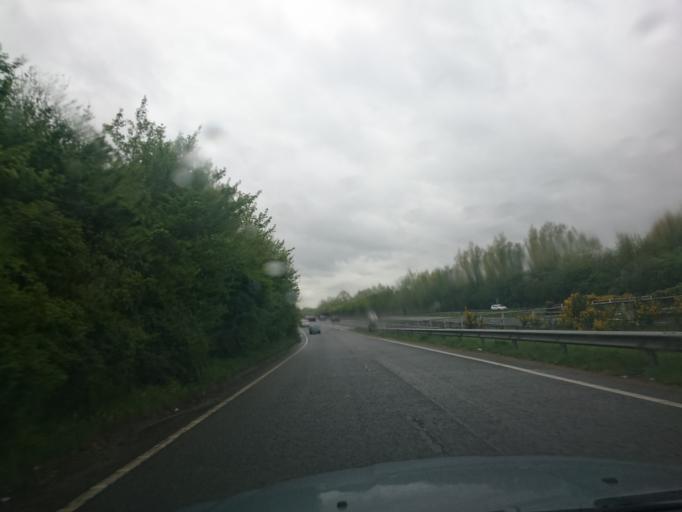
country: GB
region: England
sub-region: Surrey
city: Seale
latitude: 51.2402
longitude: -0.7358
